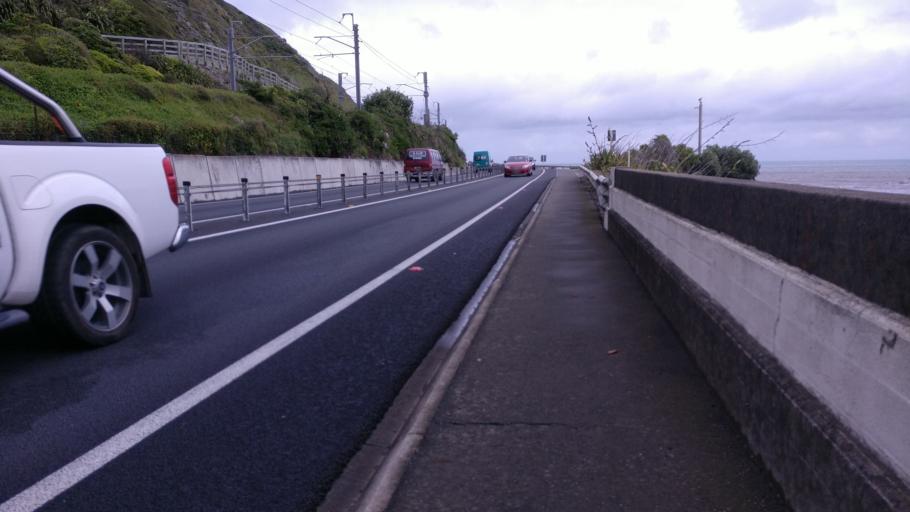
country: NZ
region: Wellington
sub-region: Kapiti Coast District
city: Paraparaumu
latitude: -41.0040
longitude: 174.9316
